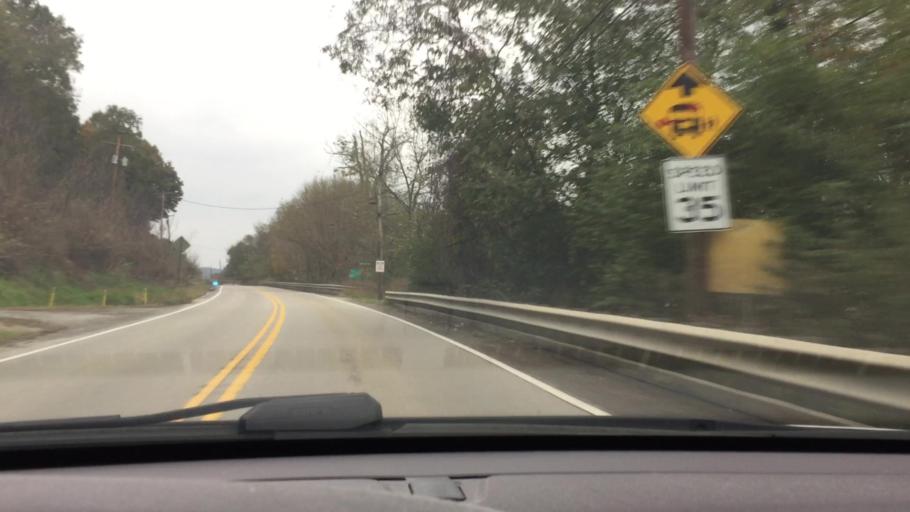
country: US
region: Pennsylvania
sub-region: Fayette County
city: Fairhope
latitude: 40.1107
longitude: -79.8527
